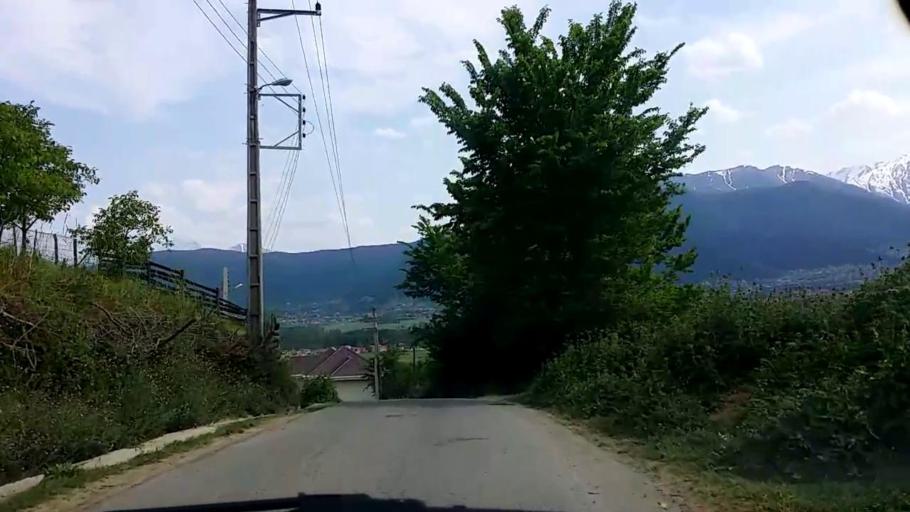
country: IR
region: Mazandaran
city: `Abbasabad
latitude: 36.5526
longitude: 51.1820
